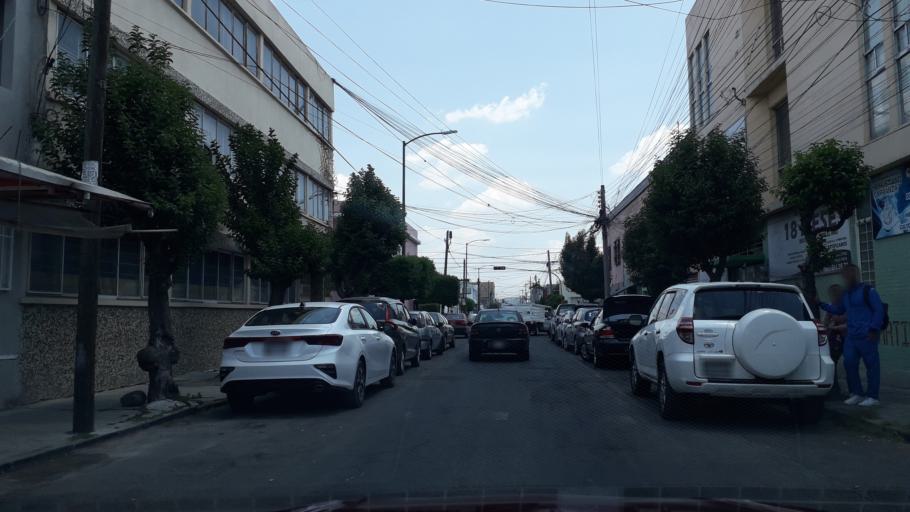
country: MX
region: Puebla
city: Puebla
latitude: 19.0362
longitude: -98.2101
